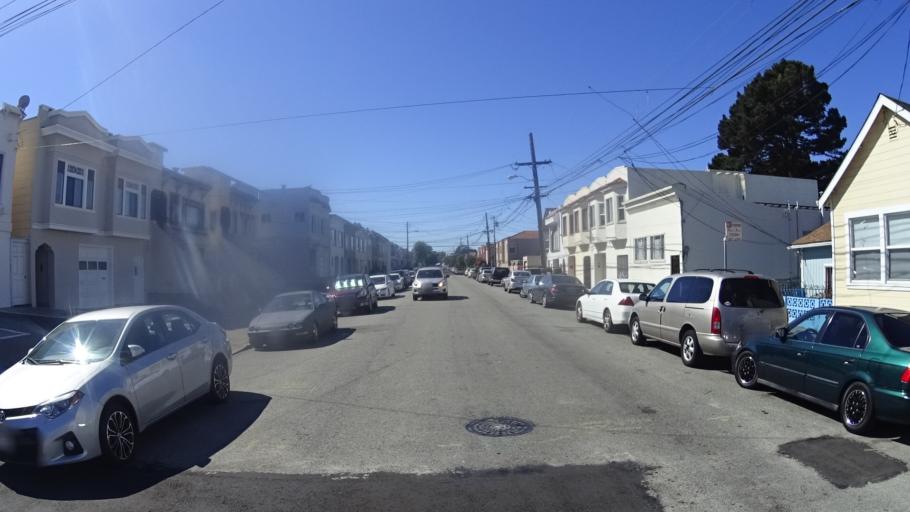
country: US
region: California
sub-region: San Mateo County
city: Daly City
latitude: 37.7087
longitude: -122.4487
